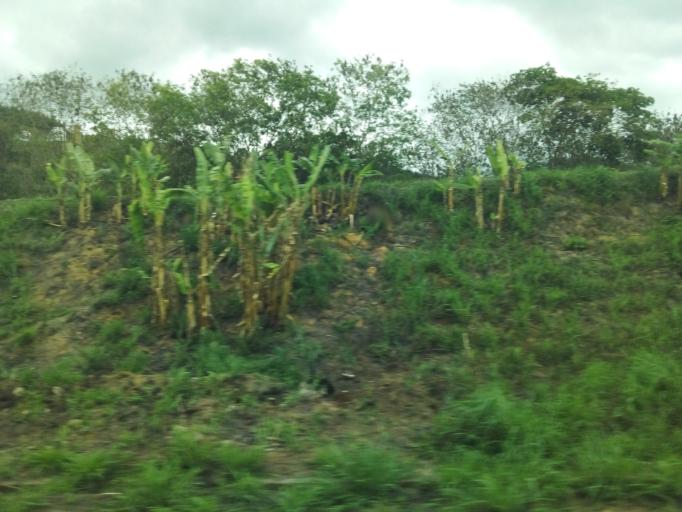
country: BR
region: Minas Gerais
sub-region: Coronel Fabriciano
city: Coronel Fabriciano
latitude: -19.5310
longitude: -42.6718
